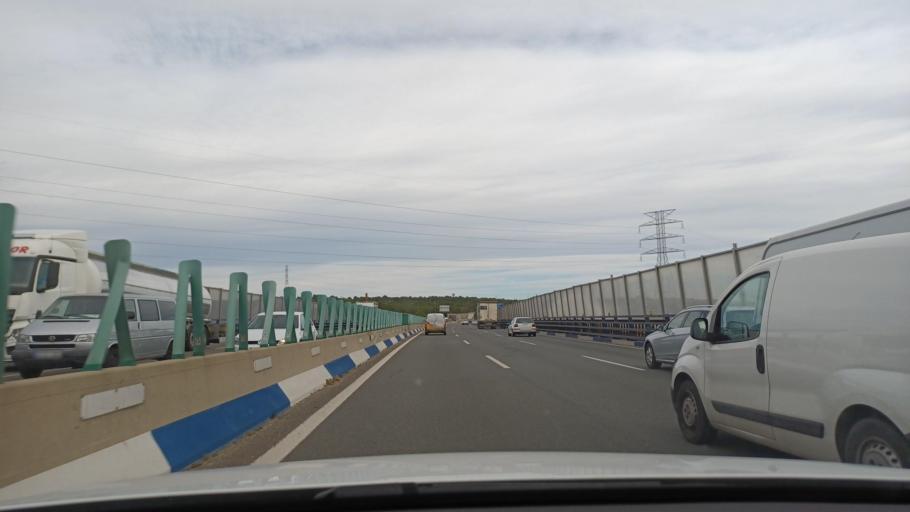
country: ES
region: Valencia
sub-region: Provincia de Valencia
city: Manises
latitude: 39.5122
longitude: -0.5017
